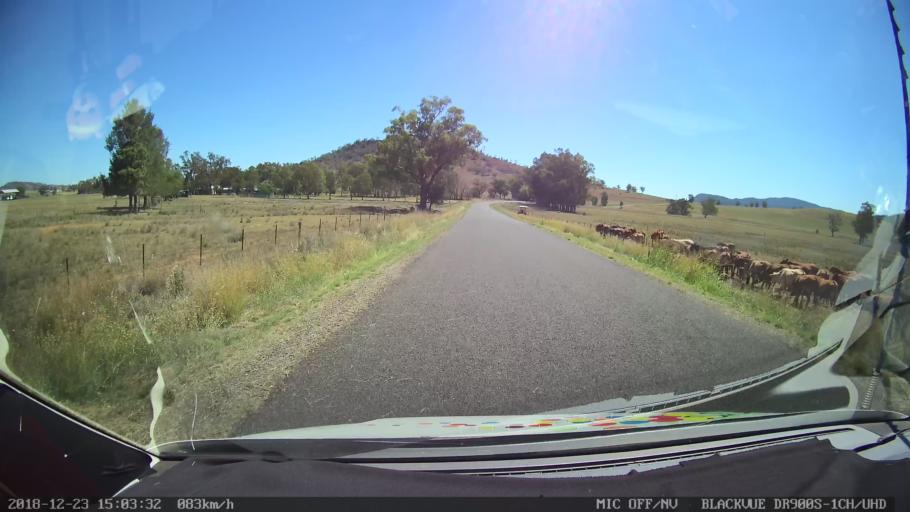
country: AU
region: New South Wales
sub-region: Tamworth Municipality
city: Manilla
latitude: -30.7394
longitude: 150.7639
